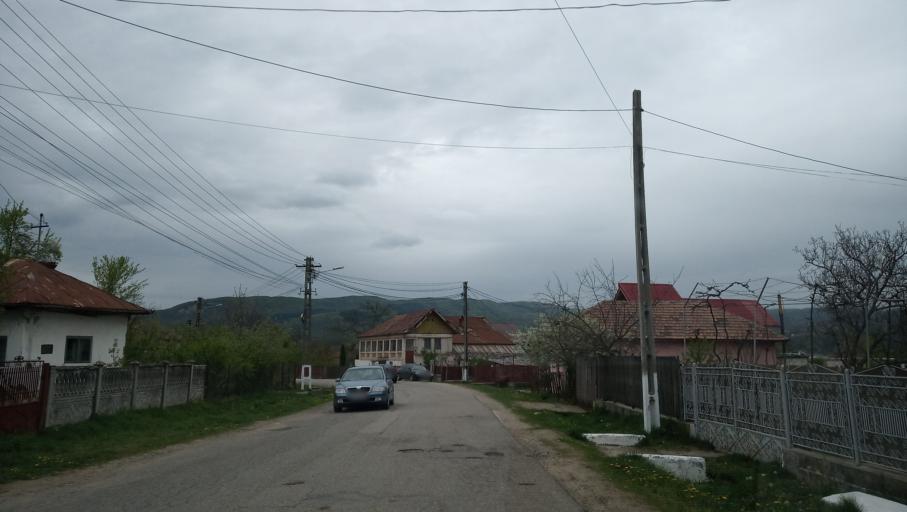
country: RO
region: Valcea
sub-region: Comuna Daesti
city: Daesti
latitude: 45.1831
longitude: 24.3834
